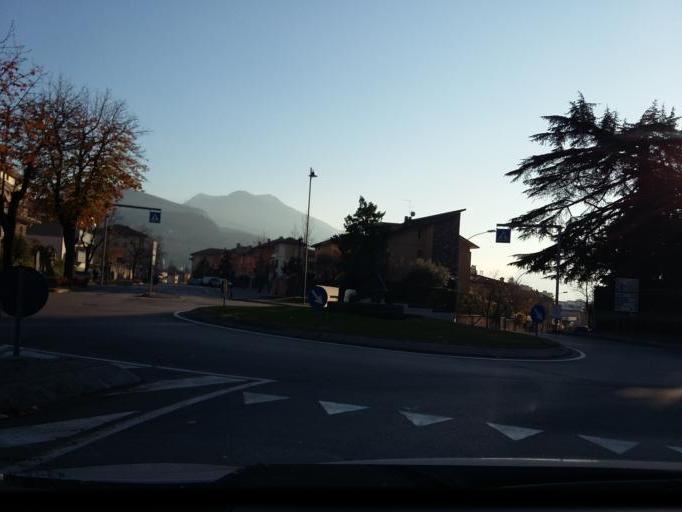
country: IT
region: Trentino-Alto Adige
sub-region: Provincia di Trento
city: Rovereto
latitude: 45.8989
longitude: 11.0423
